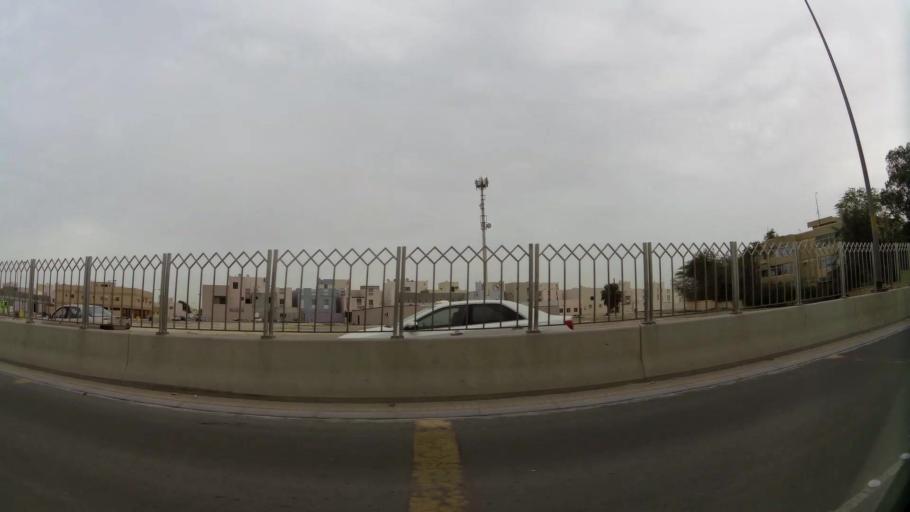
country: BH
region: Manama
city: Jidd Hafs
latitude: 26.2119
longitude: 50.5342
